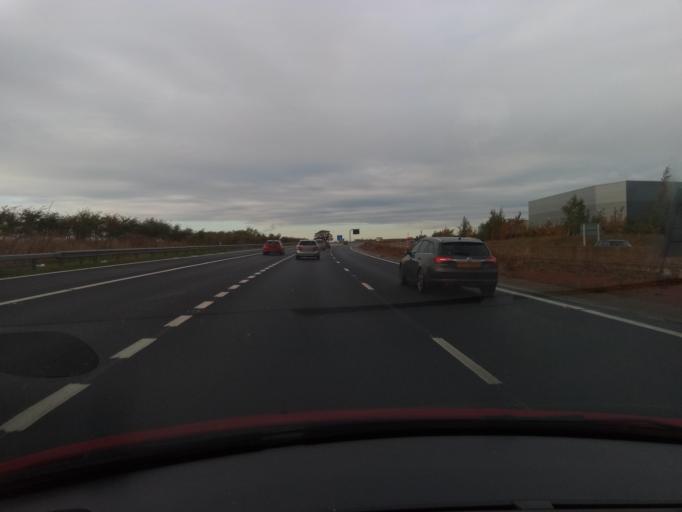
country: GB
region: England
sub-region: North Yorkshire
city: Bedale
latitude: 54.3034
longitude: -1.5695
